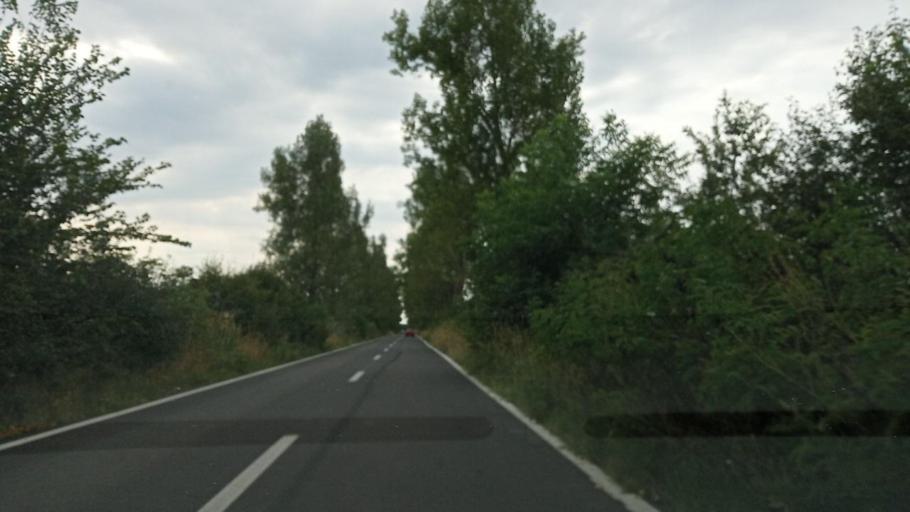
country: RO
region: Giurgiu
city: Gostinari-Vacaresti
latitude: 44.1731
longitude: 26.2163
